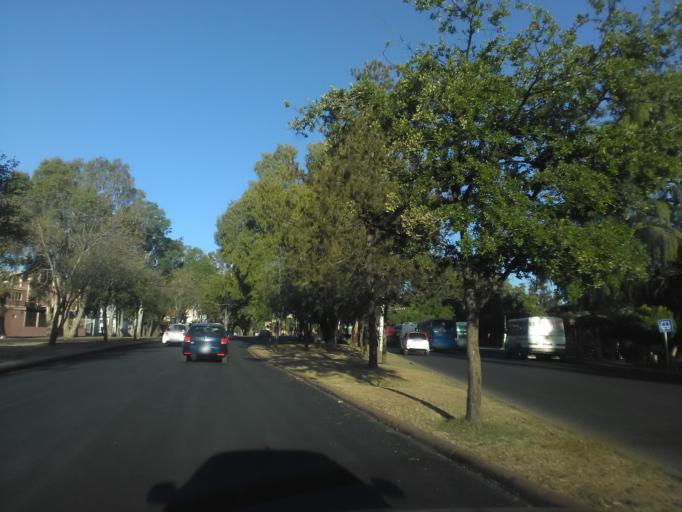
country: MX
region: Durango
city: Victoria de Durango
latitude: 24.0202
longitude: -104.6685
